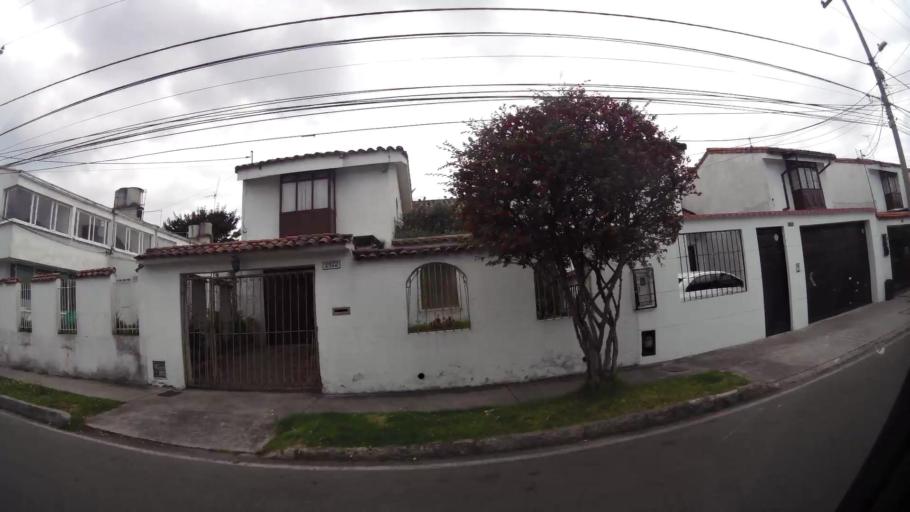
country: CO
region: Bogota D.C.
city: Barrio San Luis
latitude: 4.7132
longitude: -74.0692
